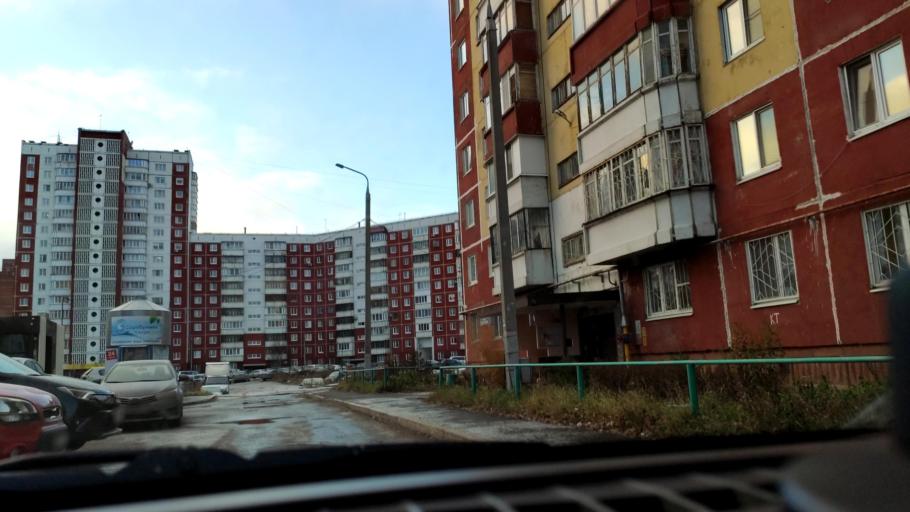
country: RU
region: Perm
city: Kondratovo
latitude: 57.9942
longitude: 56.1337
